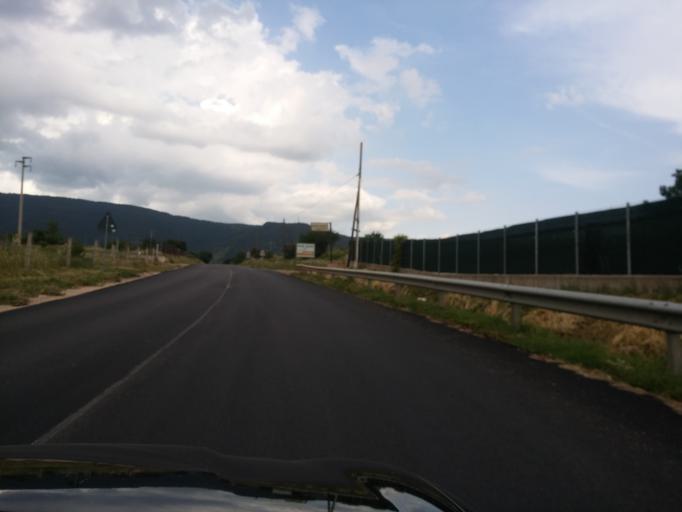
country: IT
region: Apulia
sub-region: Provincia di Foggia
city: Rignano Garganico
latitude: 41.7143
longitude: 15.5549
